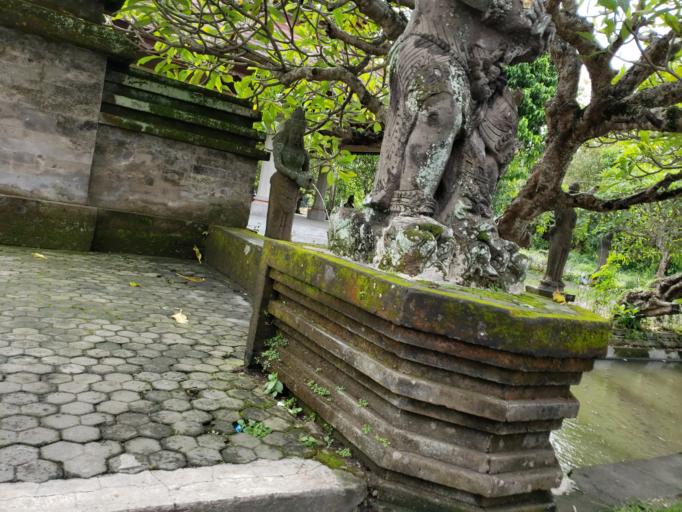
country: ID
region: Bali
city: Banjar Jabejero
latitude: -8.6062
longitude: 115.2553
